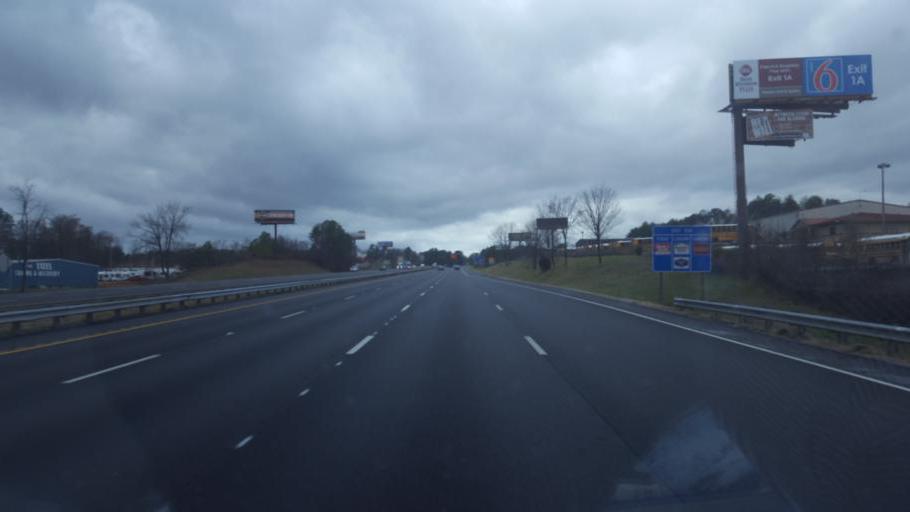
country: US
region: Georgia
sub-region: Catoosa County
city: Ringgold
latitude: 34.9112
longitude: -85.1308
